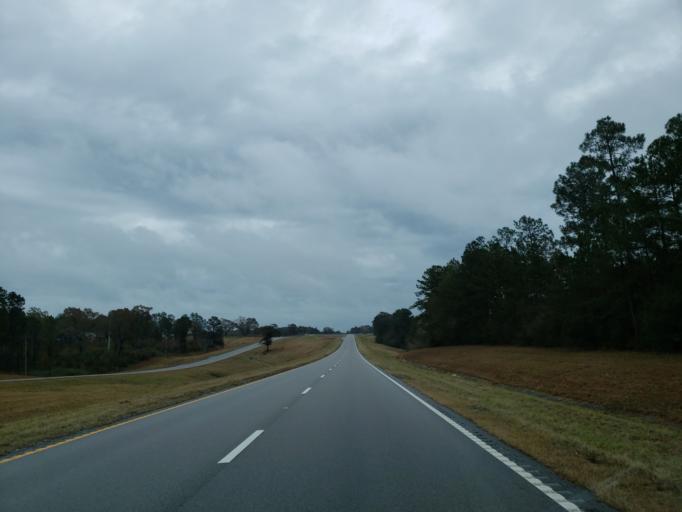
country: US
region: Mississippi
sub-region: Wayne County
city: Waynesboro
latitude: 31.6955
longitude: -88.7406
